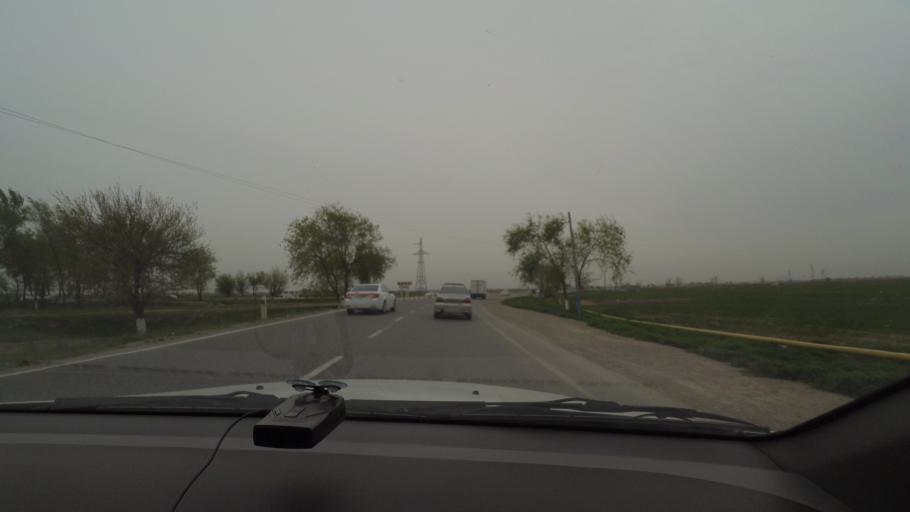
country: KZ
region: Ongtustik Qazaqstan
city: Myrzakent
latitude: 40.5624
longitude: 68.3758
